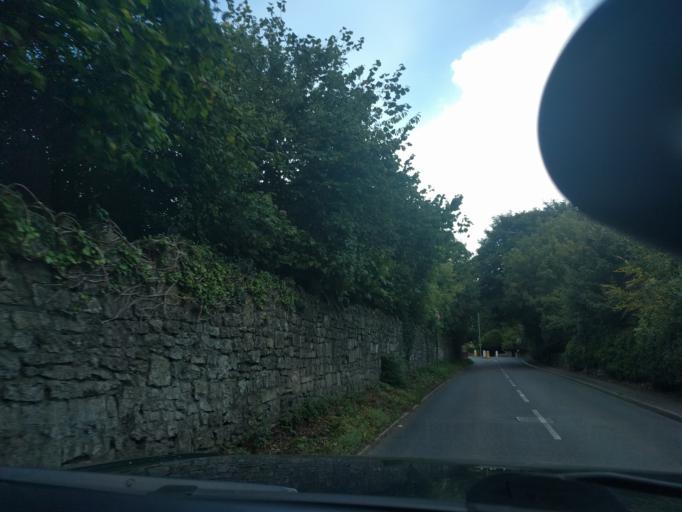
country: GB
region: England
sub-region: Bath and North East Somerset
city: Freshford
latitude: 51.3656
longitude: -2.3188
